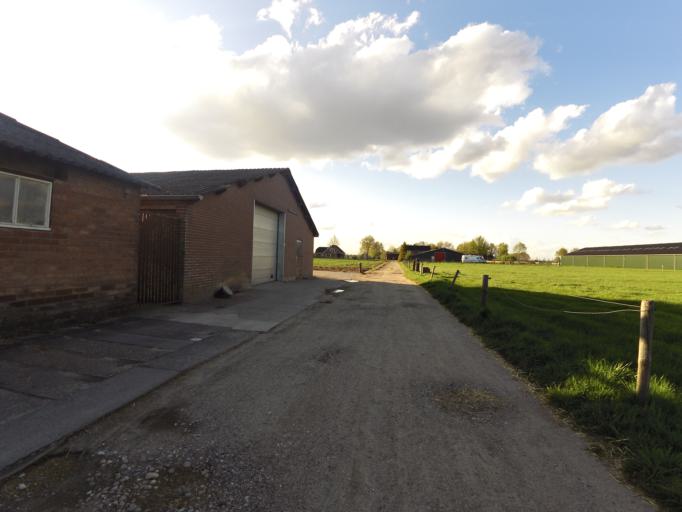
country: NL
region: Gelderland
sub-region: Gemeente Zevenaar
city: Zevenaar
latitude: 51.9531
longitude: 6.1259
